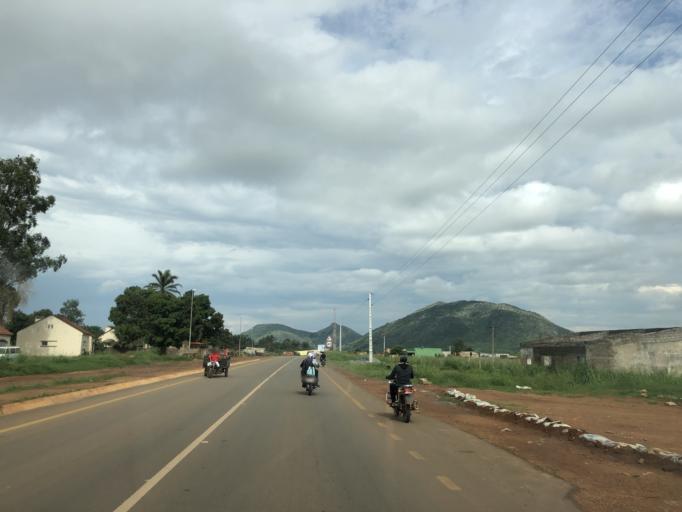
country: AO
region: Cuanza Sul
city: Uacu Cungo
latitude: -11.3505
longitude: 15.1085
